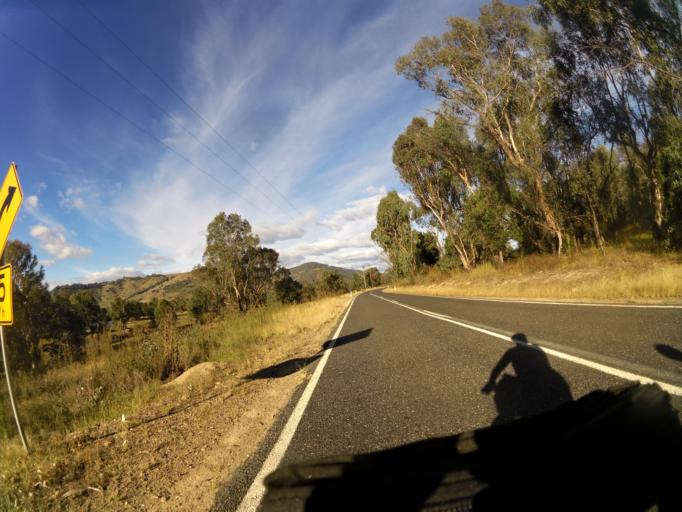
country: AU
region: New South Wales
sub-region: Greater Hume Shire
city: Holbrook
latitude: -35.9916
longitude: 147.8533
